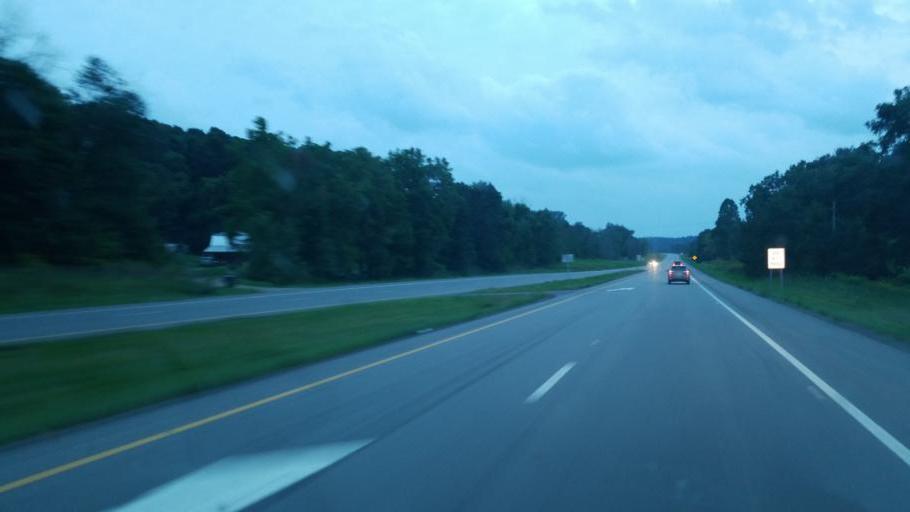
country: US
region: Ohio
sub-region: Sandusky County
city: Bellville
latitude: 40.6470
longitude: -82.5160
